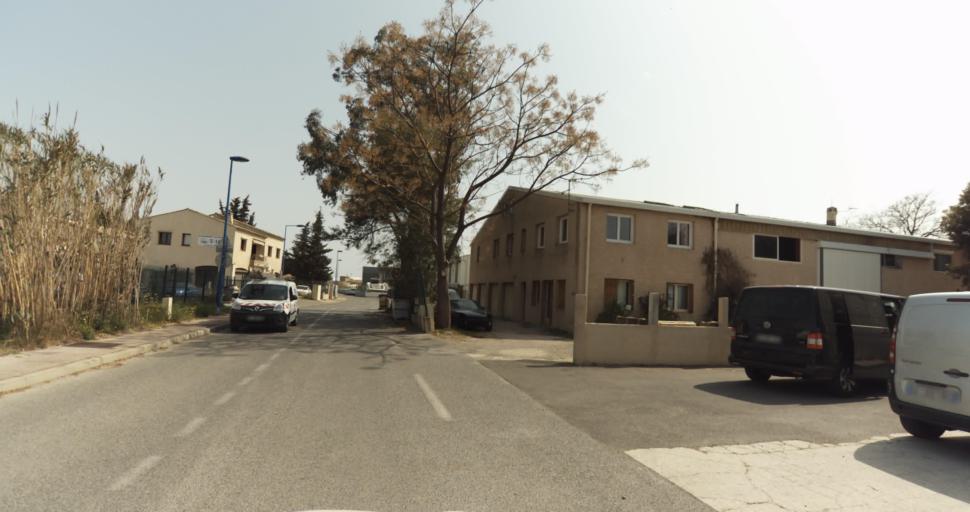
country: FR
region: Provence-Alpes-Cote d'Azur
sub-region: Departement du Var
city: Bormes-les-Mimosas
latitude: 43.1324
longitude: 6.3468
